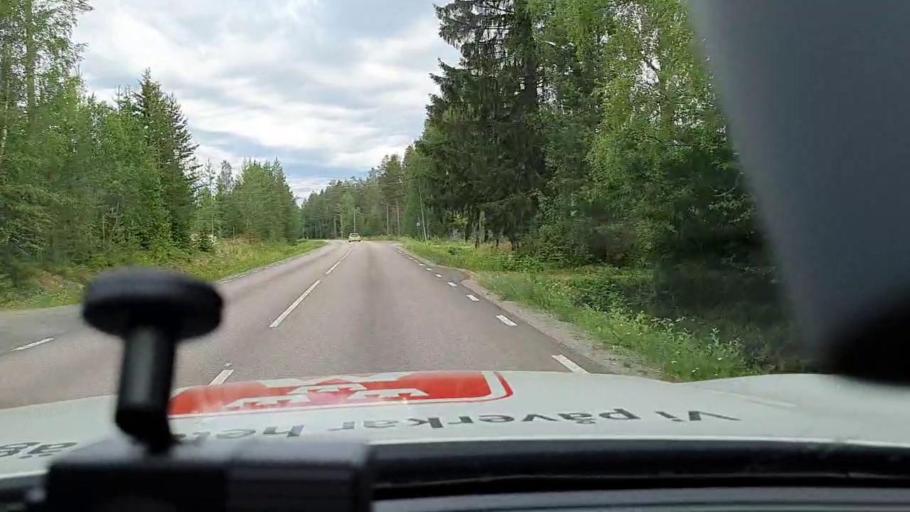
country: SE
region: Norrbotten
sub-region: Bodens Kommun
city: Saevast
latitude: 65.7242
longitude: 21.7506
